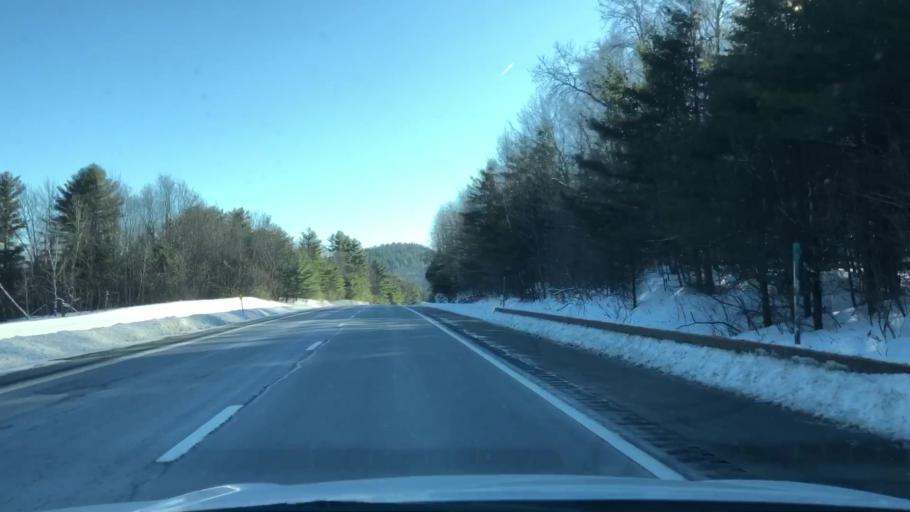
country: US
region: New York
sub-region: Warren County
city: Warrensburg
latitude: 43.7685
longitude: -73.8033
